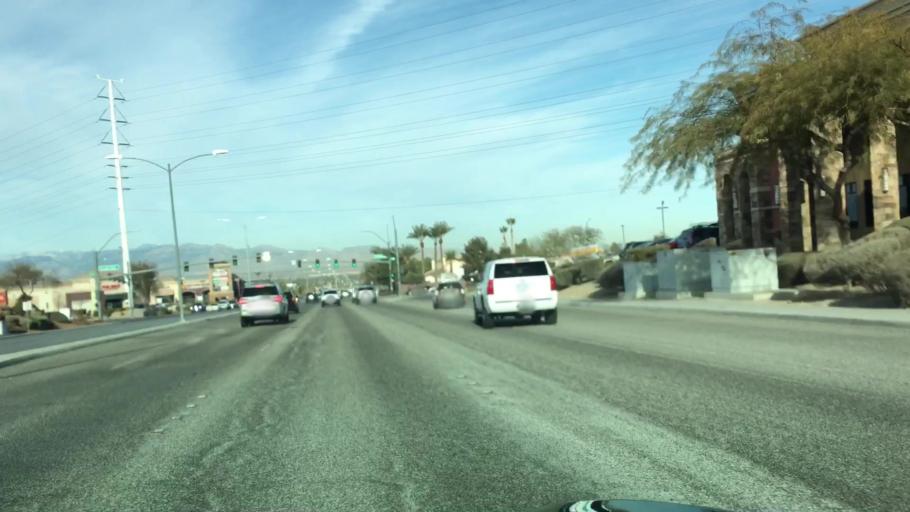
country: US
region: Nevada
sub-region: Clark County
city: Whitney
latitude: 36.0018
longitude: -115.1078
